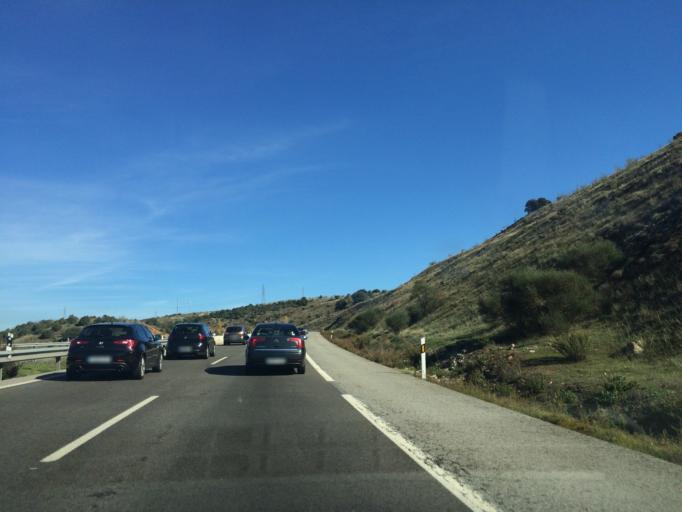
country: ES
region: Madrid
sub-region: Provincia de Madrid
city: Cabanillas de la Sierra
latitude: 40.8098
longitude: -3.6190
